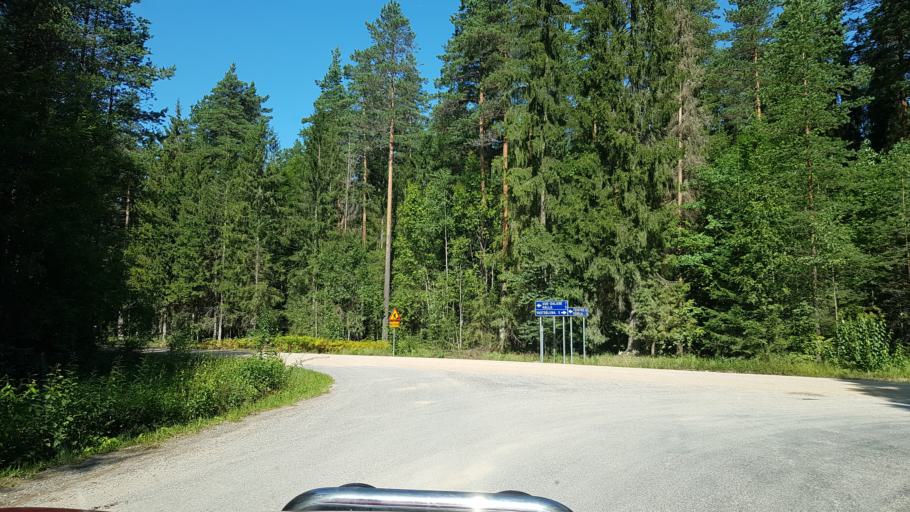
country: EE
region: Vorumaa
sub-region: Voru linn
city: Voru
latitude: 57.7349
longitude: 27.2040
